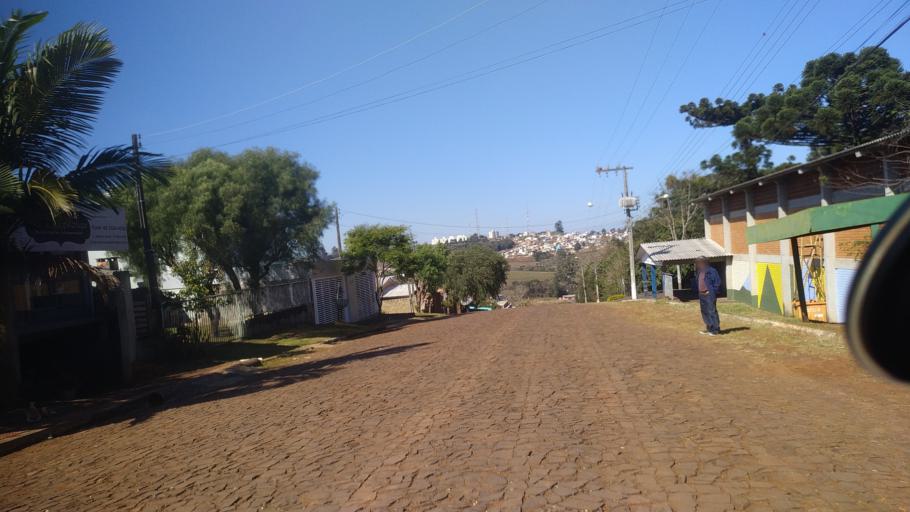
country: BR
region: Santa Catarina
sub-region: Chapeco
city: Chapeco
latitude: -27.0904
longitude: -52.5876
